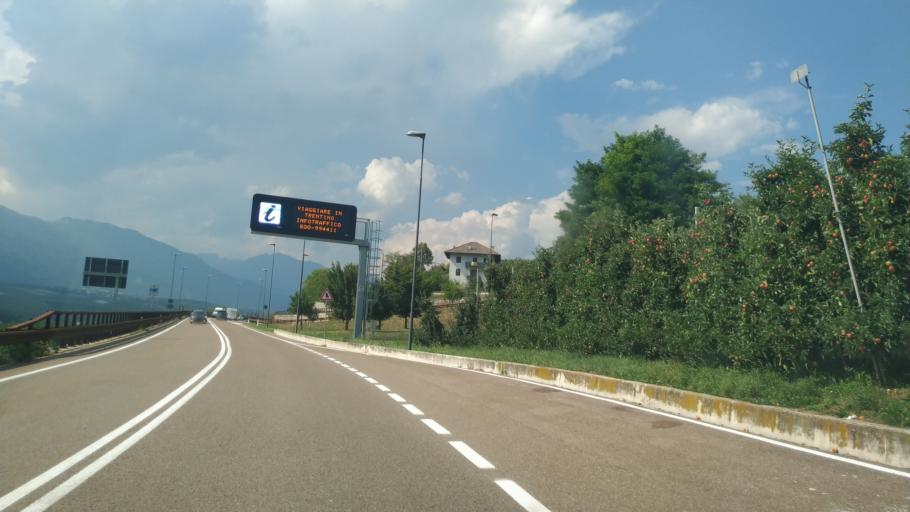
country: IT
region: Trentino-Alto Adige
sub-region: Provincia di Trento
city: Taio
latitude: 46.3060
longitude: 11.0706
